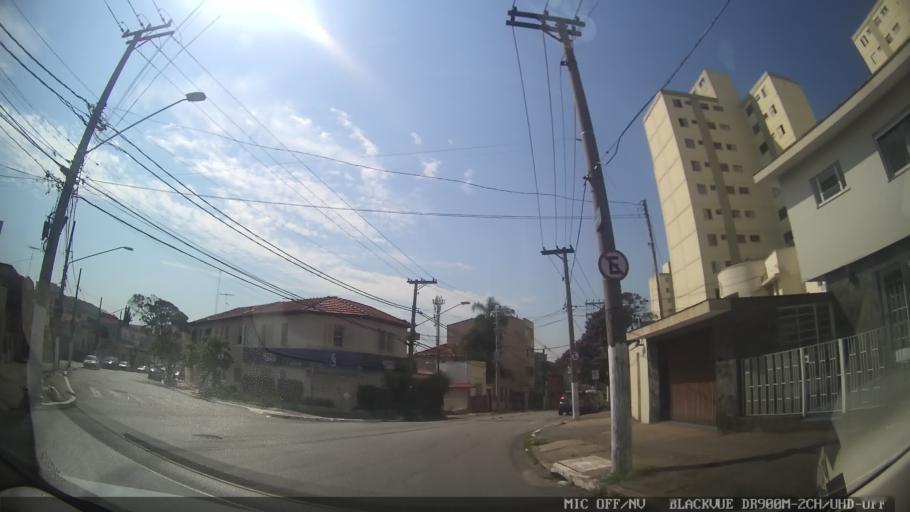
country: BR
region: Sao Paulo
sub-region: Sao Paulo
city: Sao Paulo
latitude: -23.5752
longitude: -46.6158
